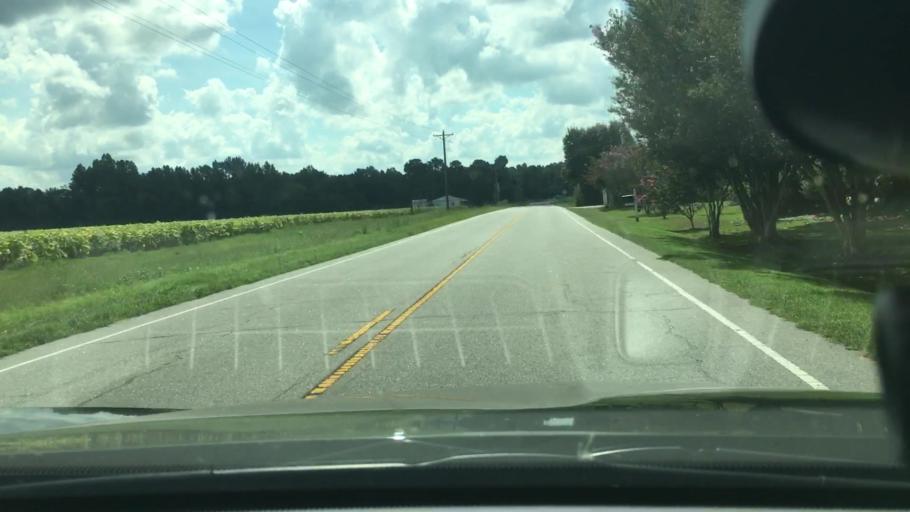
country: US
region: North Carolina
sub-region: Edgecombe County
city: Pinetops
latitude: 35.7495
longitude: -77.5437
